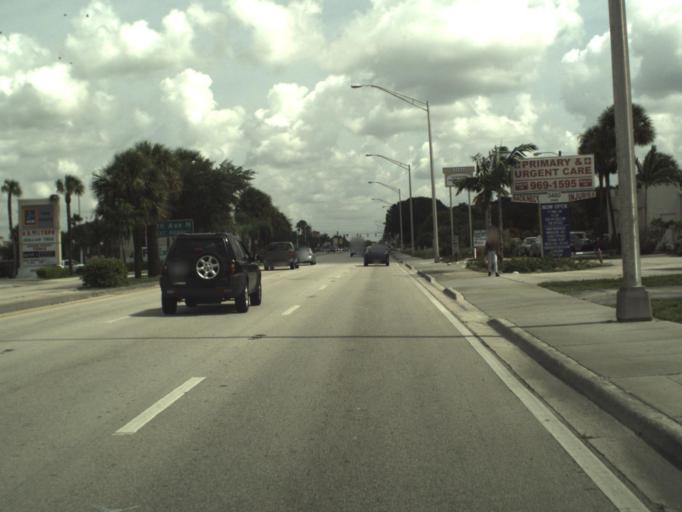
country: US
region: Florida
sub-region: Palm Beach County
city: Palm Springs
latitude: 26.6250
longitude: -80.0887
